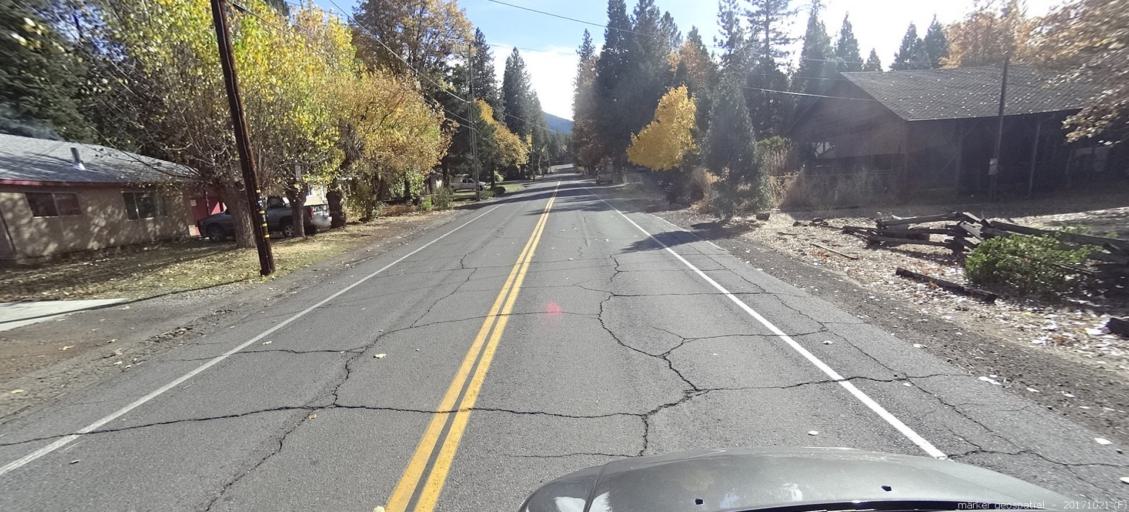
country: US
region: California
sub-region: Shasta County
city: Burney
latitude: 40.8779
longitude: -121.6575
